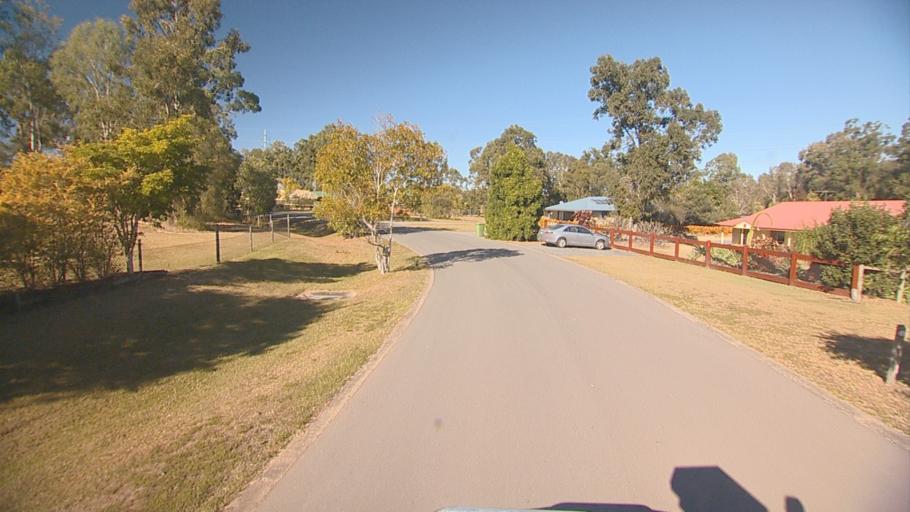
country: AU
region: Queensland
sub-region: Logan
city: North Maclean
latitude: -27.7349
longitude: 152.9679
